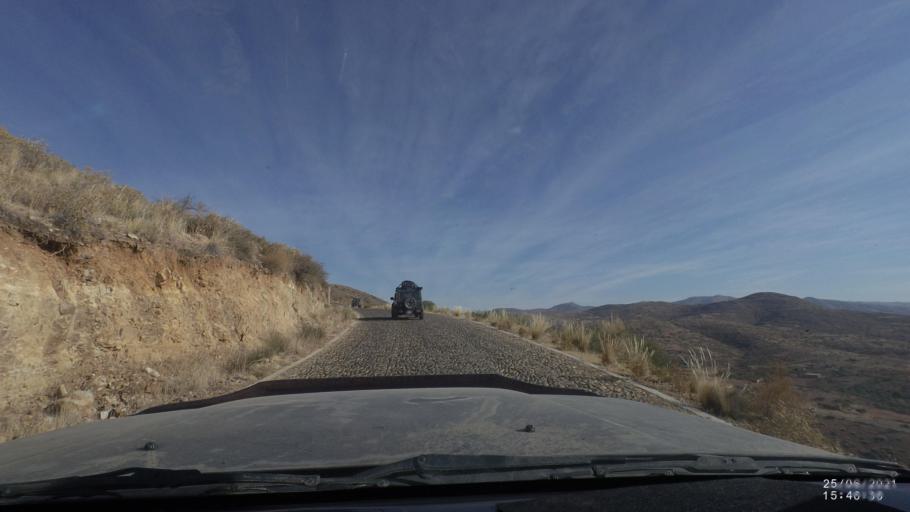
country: BO
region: Cochabamba
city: Cliza
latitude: -17.6617
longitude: -65.9081
